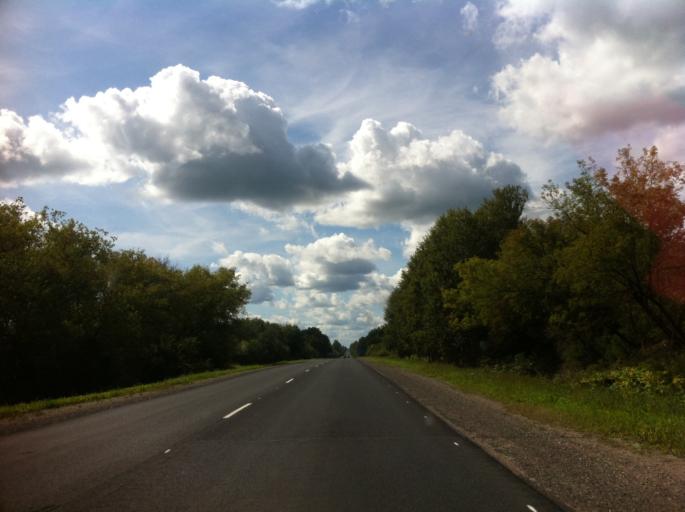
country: RU
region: Pskov
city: Izborsk
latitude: 57.7286
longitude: 27.9651
